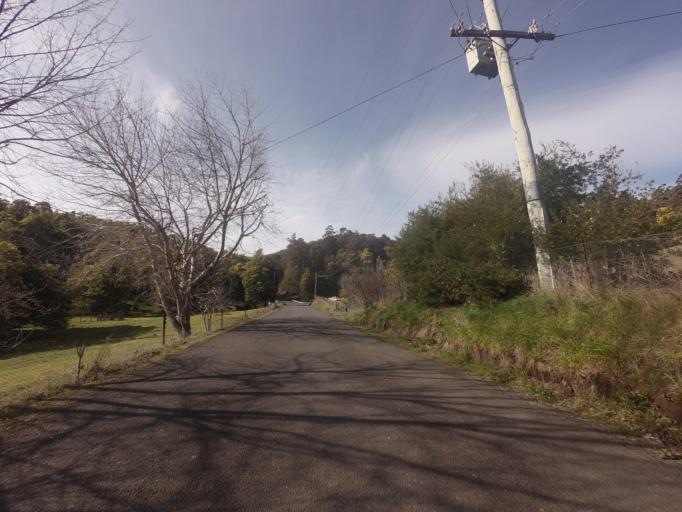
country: AU
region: Tasmania
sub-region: Huon Valley
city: Cygnet
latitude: -43.1748
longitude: 147.1556
